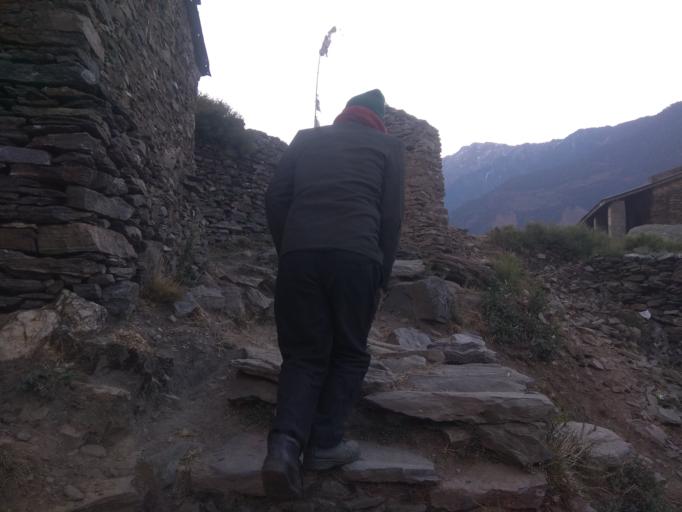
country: NP
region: Mid Western
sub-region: Bheri Zone
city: Dailekh
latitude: 29.2836
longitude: 81.7199
